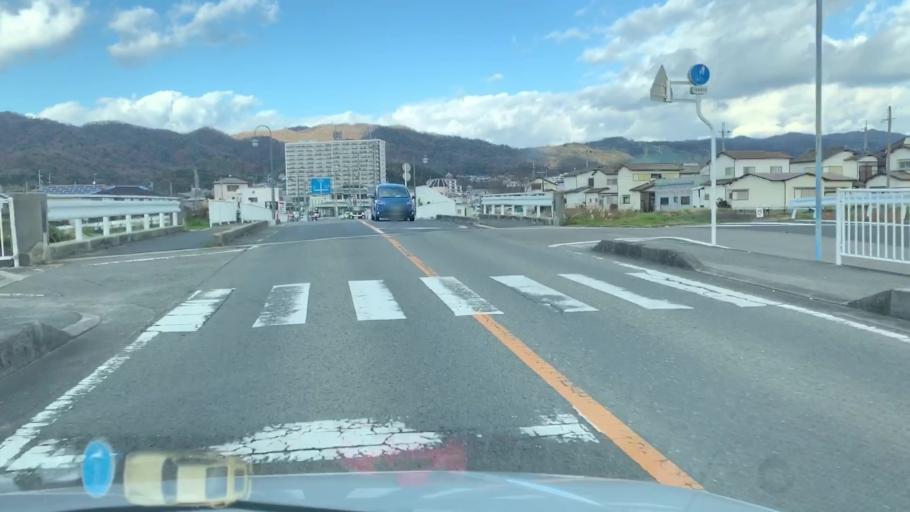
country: JP
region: Wakayama
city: Iwade
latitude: 34.2703
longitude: 135.2861
